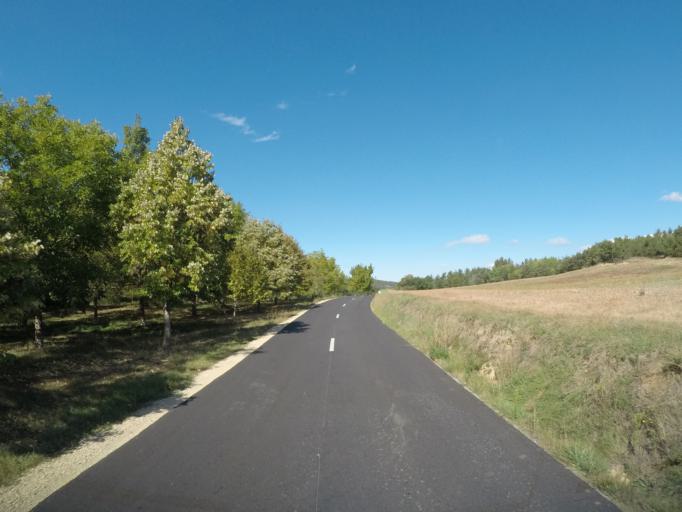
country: FR
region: Provence-Alpes-Cote d'Azur
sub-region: Departement des Alpes-de-Haute-Provence
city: Mallemoisson
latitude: 44.0141
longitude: 6.1822
